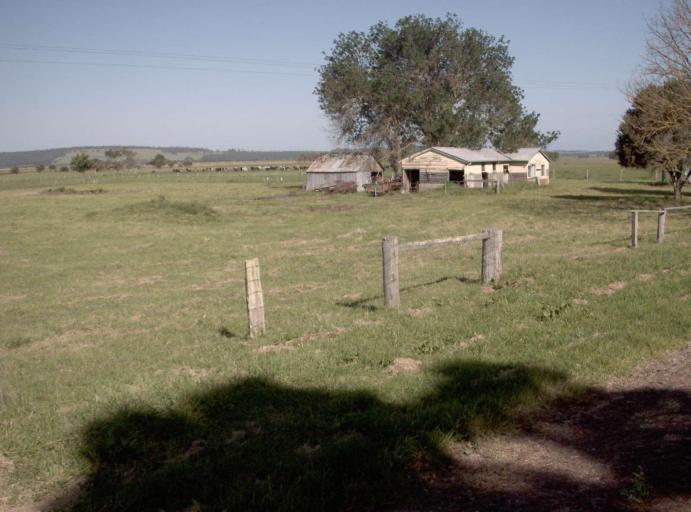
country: AU
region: Victoria
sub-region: East Gippsland
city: Lakes Entrance
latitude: -37.7459
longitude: 148.5162
